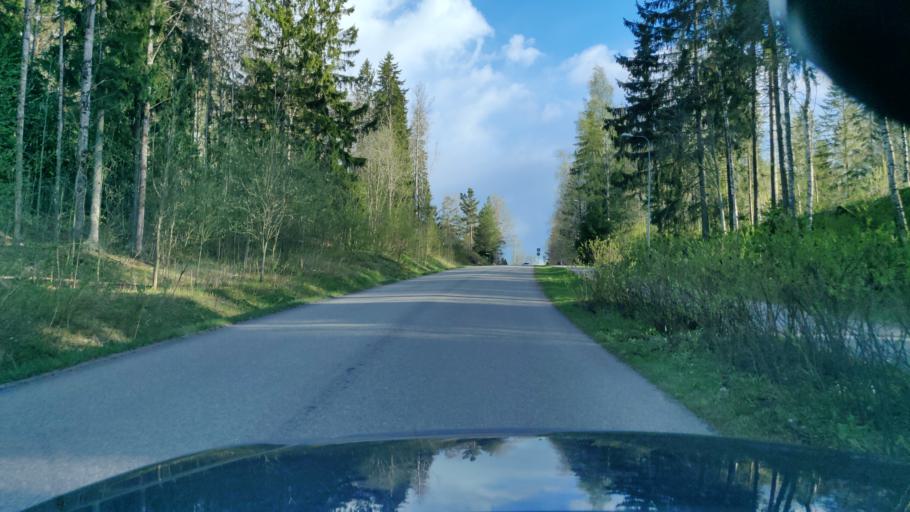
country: FI
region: Uusimaa
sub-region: Helsinki
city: Nurmijaervi
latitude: 60.3735
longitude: 24.7544
